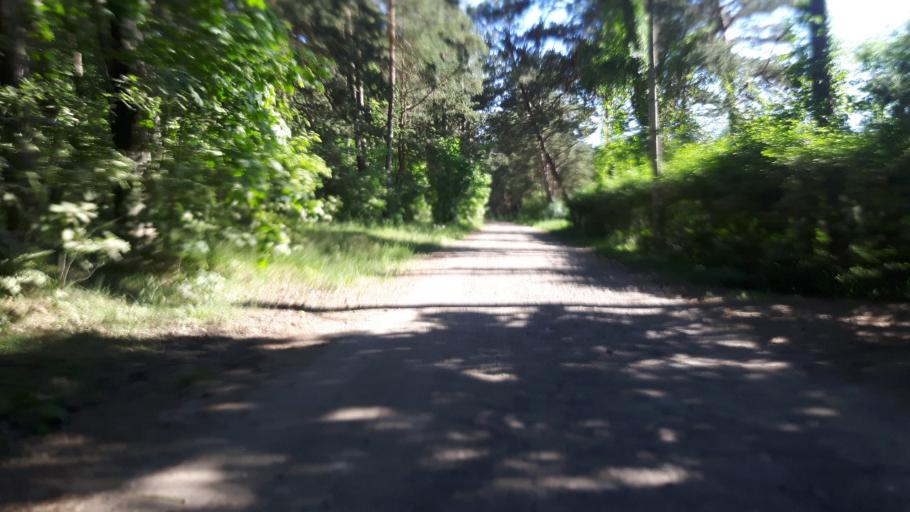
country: LV
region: Salacgrivas
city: Salacgriva
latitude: 57.7425
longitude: 24.3522
